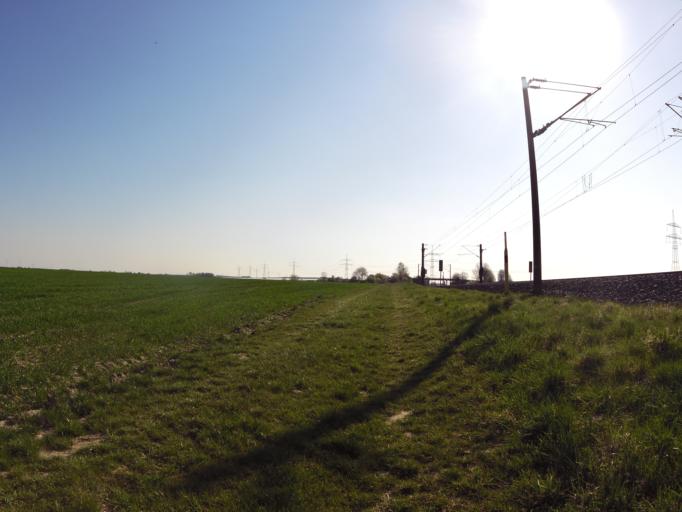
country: DE
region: Bavaria
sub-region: Regierungsbezirk Unterfranken
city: Oberpleichfeld
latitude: 49.8366
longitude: 10.0963
